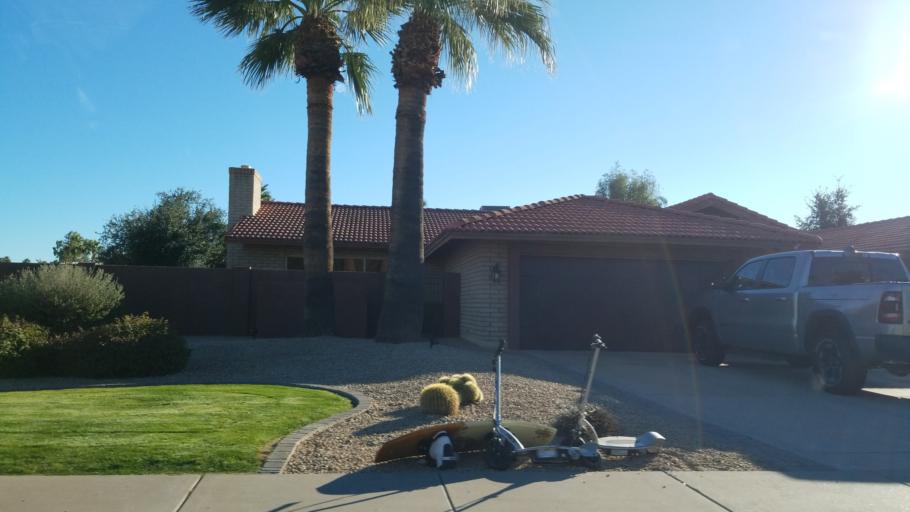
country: US
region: Arizona
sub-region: Maricopa County
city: Paradise Valley
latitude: 33.5940
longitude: -111.9662
